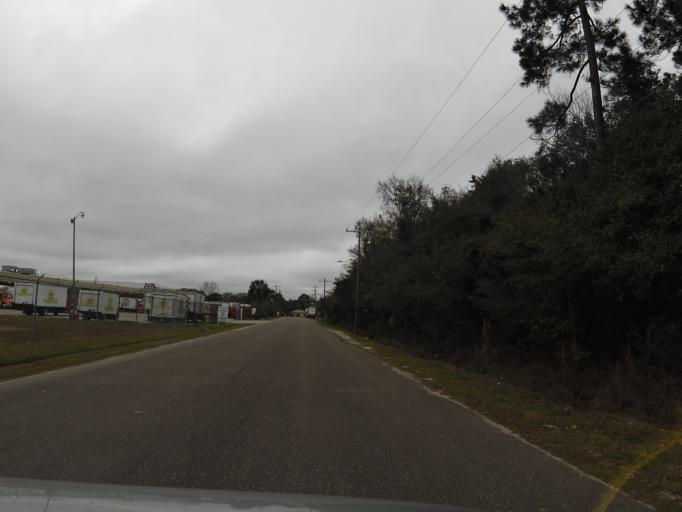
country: US
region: Florida
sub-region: Duval County
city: Jacksonville
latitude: 30.3657
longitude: -81.7123
